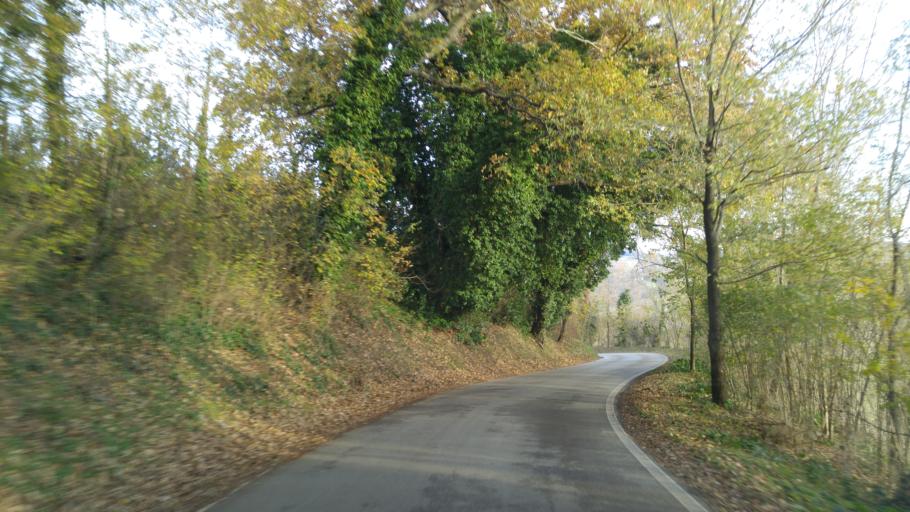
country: IT
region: The Marches
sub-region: Provincia di Pesaro e Urbino
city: Fenile
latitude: 43.8265
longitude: 12.9427
